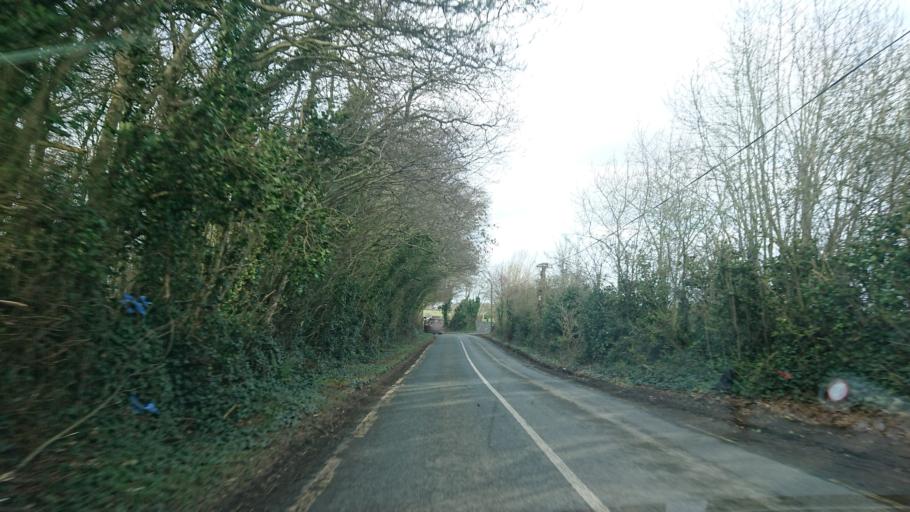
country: IE
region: Leinster
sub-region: Kildare
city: Naas
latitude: 53.1803
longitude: -6.6373
